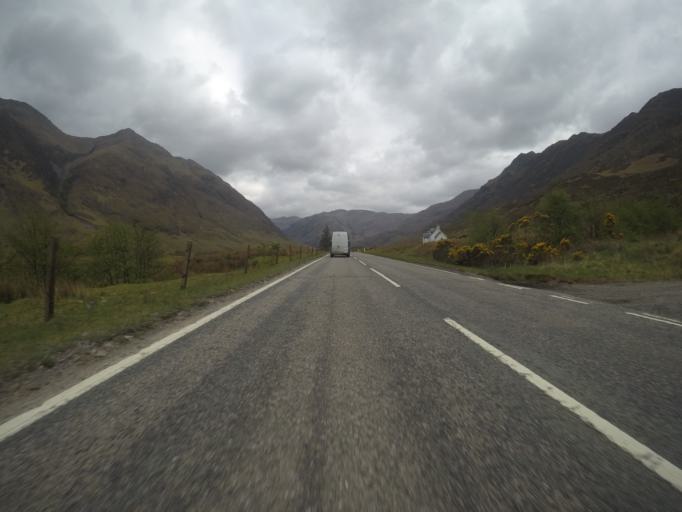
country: GB
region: Scotland
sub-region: Highland
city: Fort William
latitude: 57.1959
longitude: -5.3896
